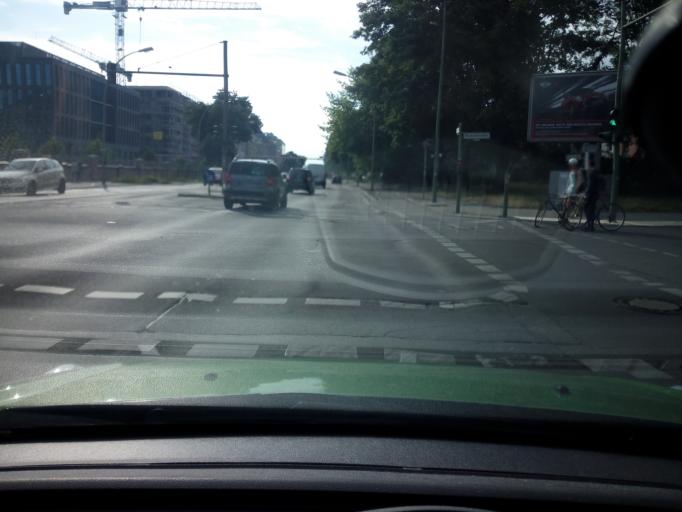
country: DE
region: Berlin
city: Treptow Bezirk
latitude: 52.5005
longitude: 13.4554
